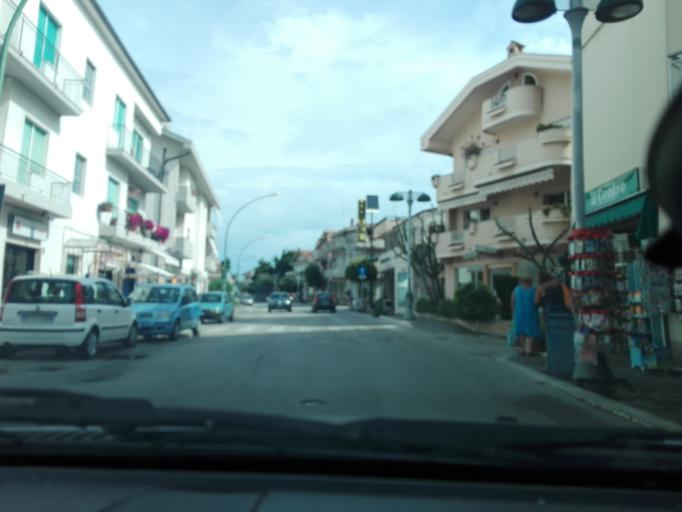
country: IT
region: Abruzzo
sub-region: Provincia di Teramo
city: Pineto
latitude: 42.6121
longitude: 14.0631
